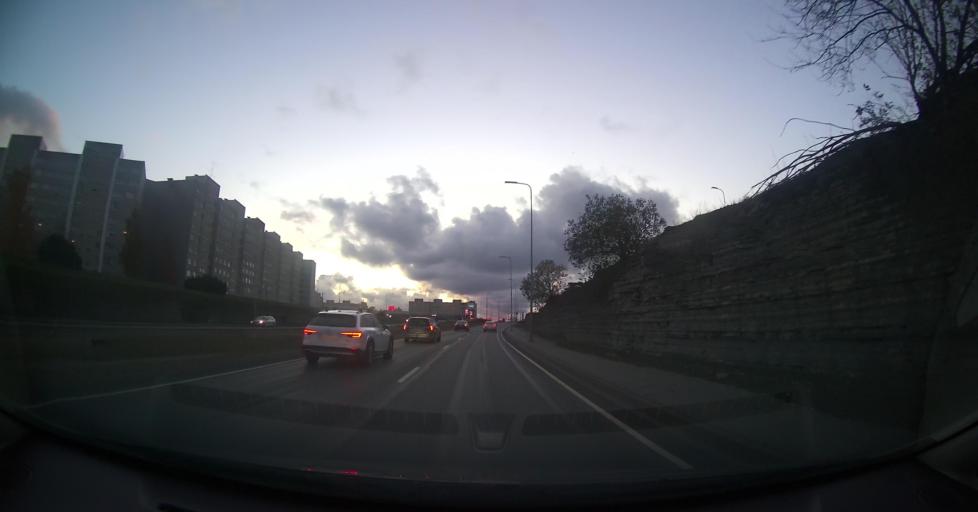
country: EE
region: Harju
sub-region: Tallinna linn
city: Kose
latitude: 59.4428
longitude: 24.8827
